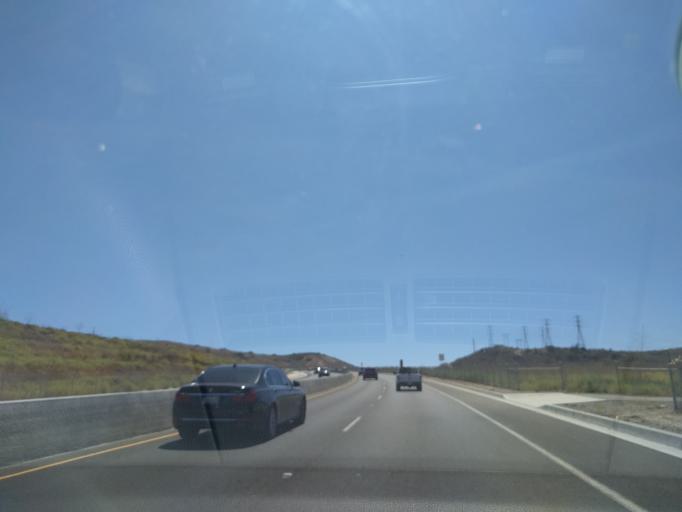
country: US
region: California
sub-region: Orange County
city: San Juan Capistrano
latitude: 33.4869
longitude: -117.6117
